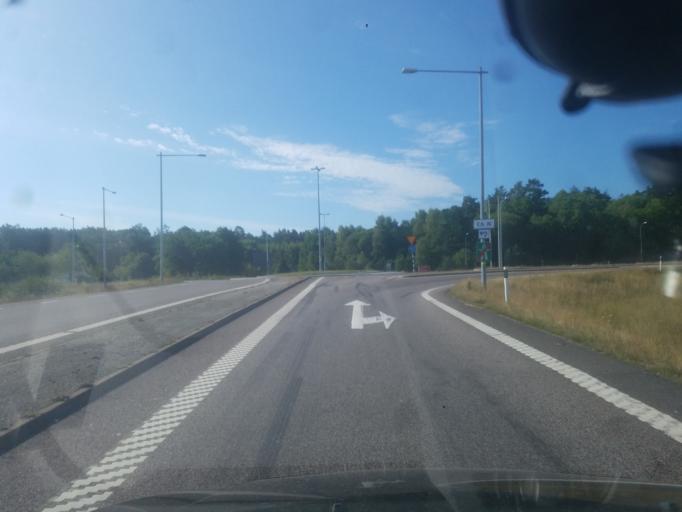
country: SE
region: Vaestra Goetaland
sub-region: Stenungsunds Kommun
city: Stora Hoga
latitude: 58.0260
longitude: 11.8498
